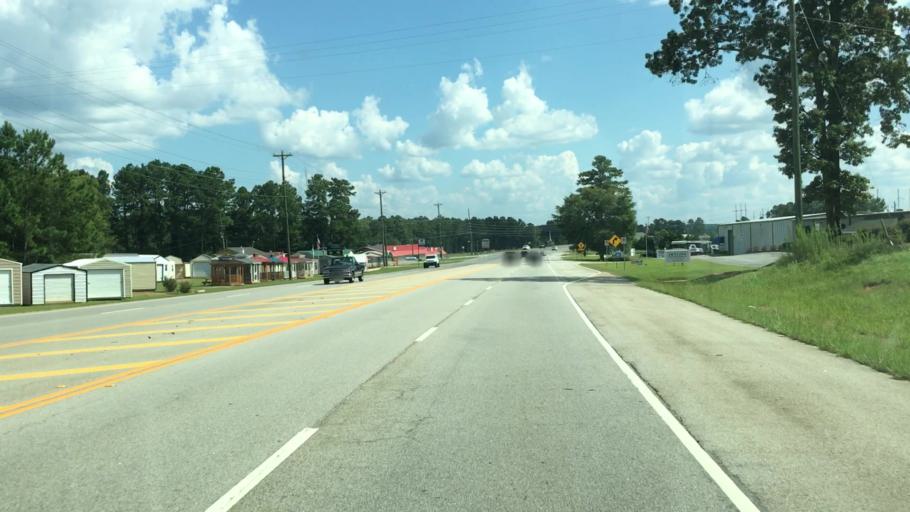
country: US
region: Georgia
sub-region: Baldwin County
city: Milledgeville
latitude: 33.2081
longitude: -83.2979
